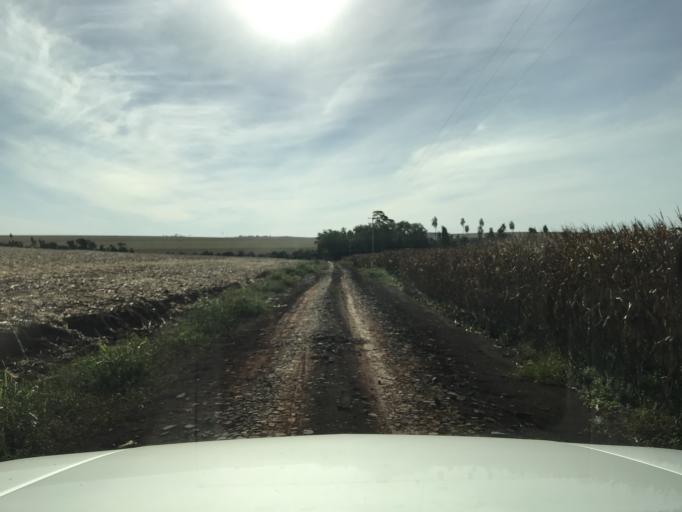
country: BR
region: Parana
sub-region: Palotina
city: Palotina
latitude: -24.2557
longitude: -53.7511
